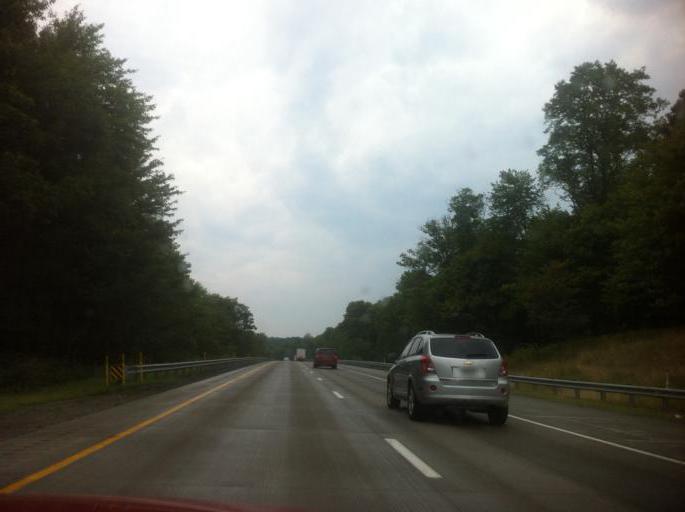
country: US
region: Pennsylvania
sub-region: Jefferson County
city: Falls Creek
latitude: 41.1564
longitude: -78.8163
